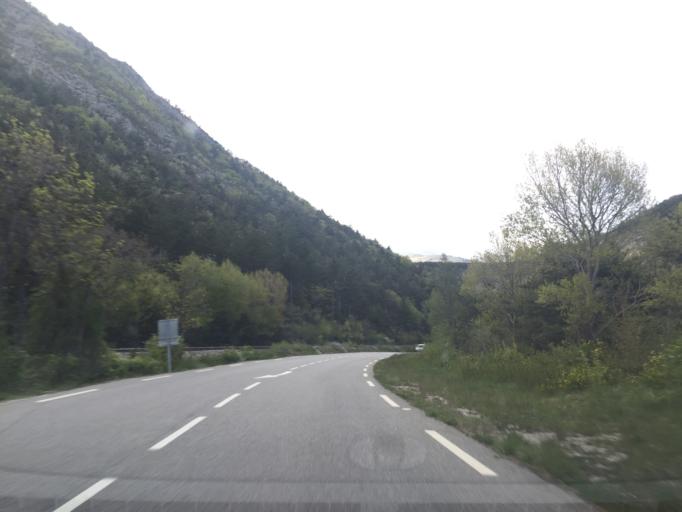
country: FR
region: Provence-Alpes-Cote d'Azur
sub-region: Departement des Hautes-Alpes
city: Veynes
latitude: 44.5432
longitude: 5.7781
